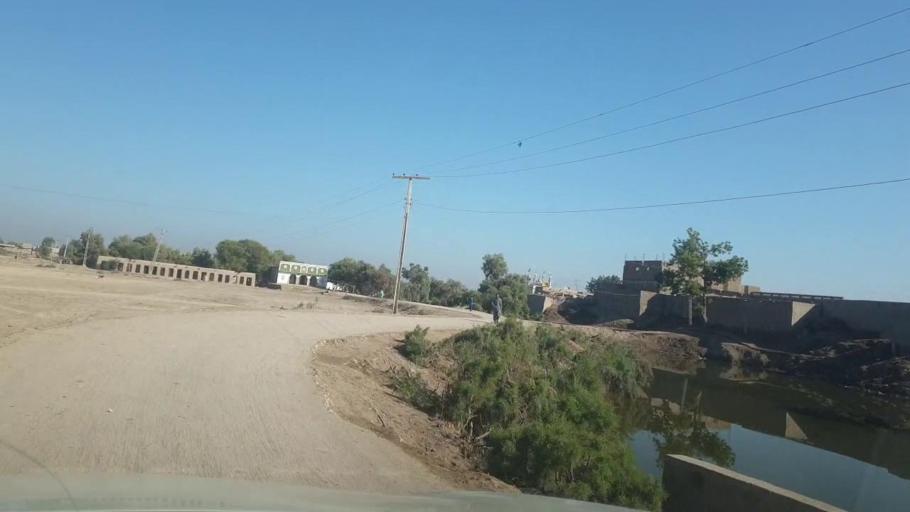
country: PK
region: Sindh
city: Bhan
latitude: 26.5438
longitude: 67.6597
